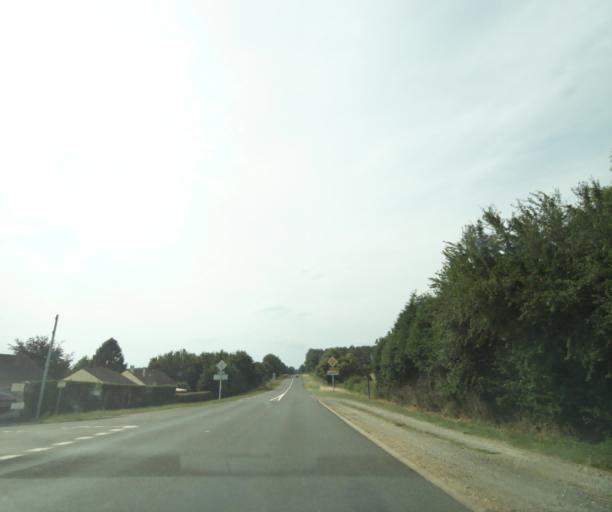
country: FR
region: Pays de la Loire
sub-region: Departement de la Sarthe
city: Marigne-Laille
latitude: 47.7939
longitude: 0.3360
